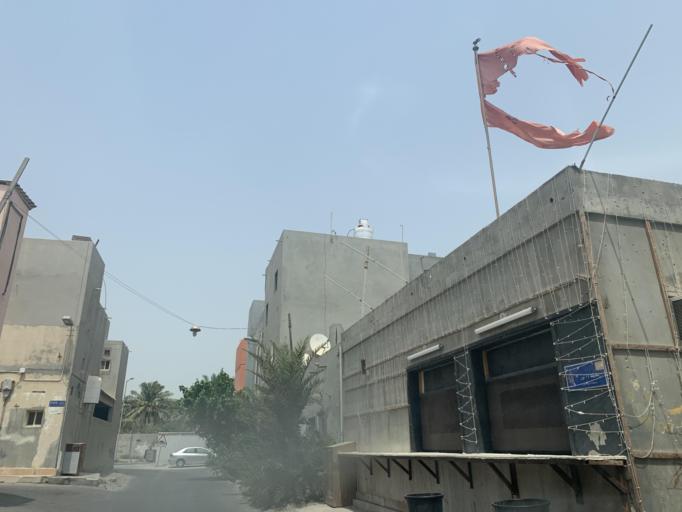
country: BH
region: Manama
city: Jidd Hafs
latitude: 26.1964
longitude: 50.4653
